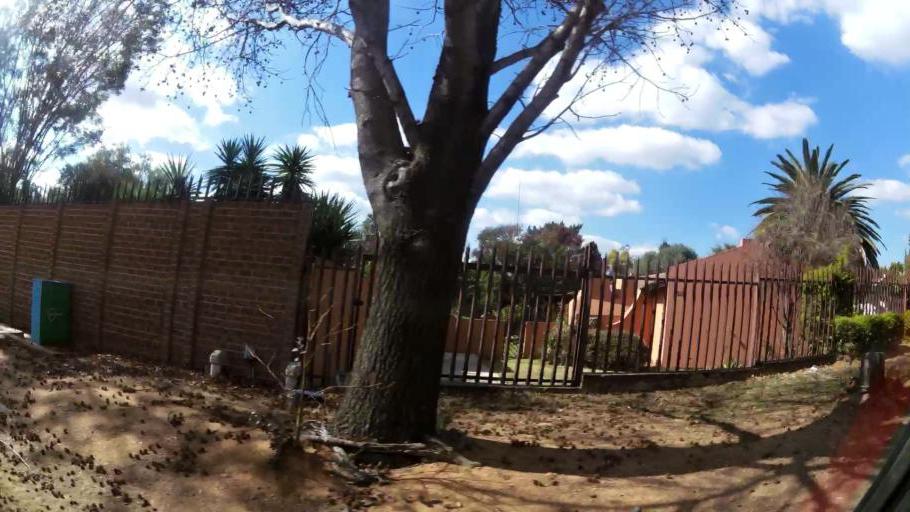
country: ZA
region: Gauteng
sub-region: City of Johannesburg Metropolitan Municipality
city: Roodepoort
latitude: -26.0750
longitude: 27.9693
